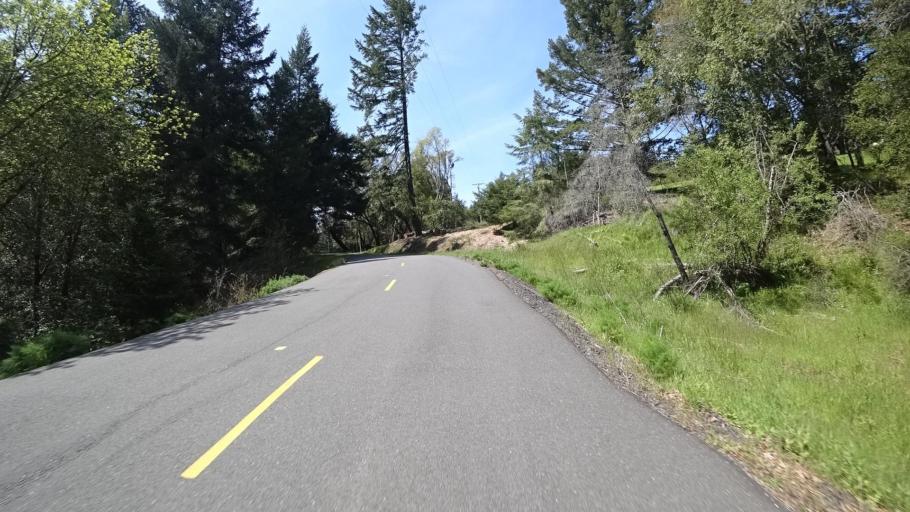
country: US
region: California
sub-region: Humboldt County
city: Redway
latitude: 40.3485
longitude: -123.7130
